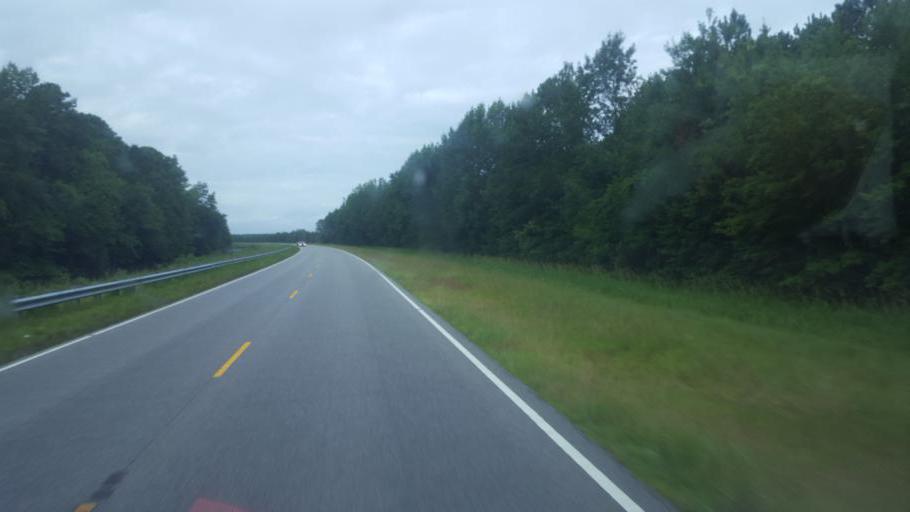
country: US
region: North Carolina
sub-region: Tyrrell County
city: Columbia
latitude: 35.9320
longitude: -76.1485
